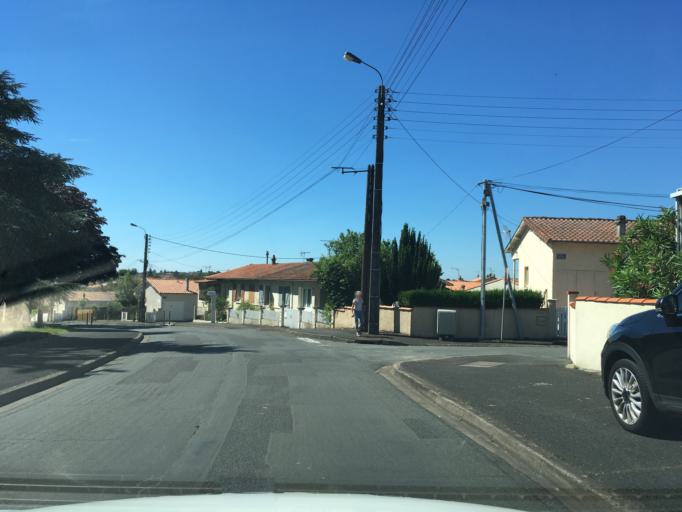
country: FR
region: Poitou-Charentes
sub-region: Departement des Deux-Sevres
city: Niort
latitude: 46.3242
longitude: -0.4390
